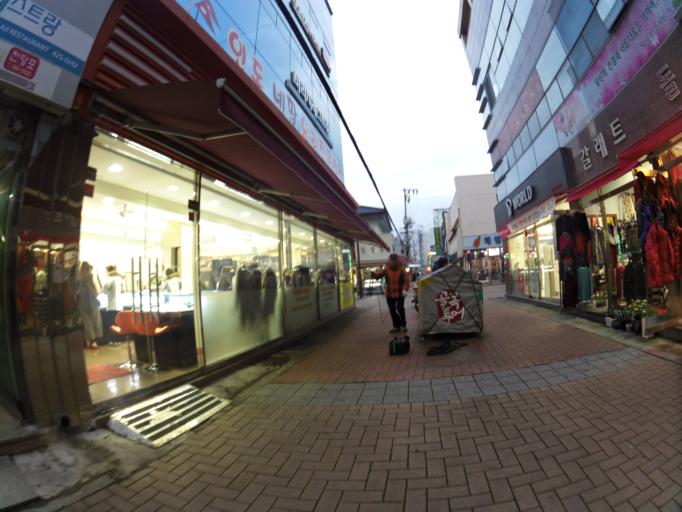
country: KR
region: Daegu
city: Daegu
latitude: 35.8733
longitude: 128.5956
